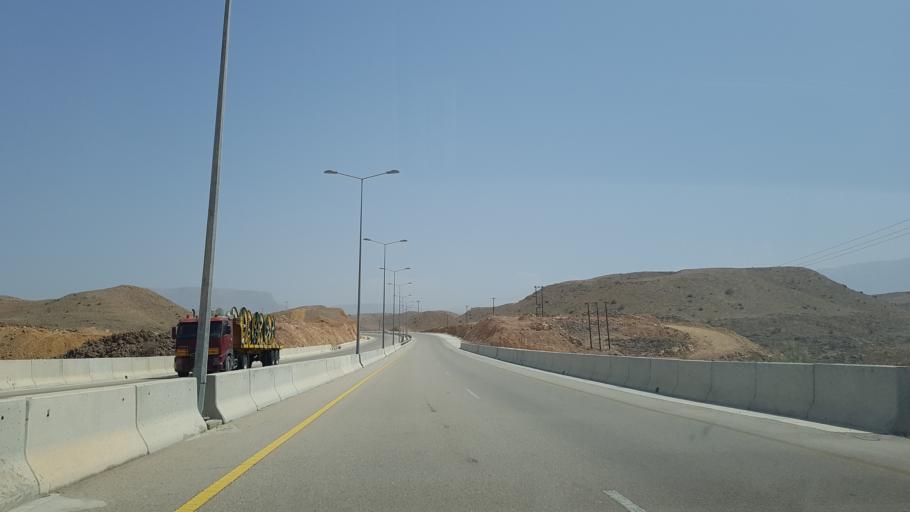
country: OM
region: Muhafazat Masqat
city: Muscat
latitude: 23.1347
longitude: 58.9720
